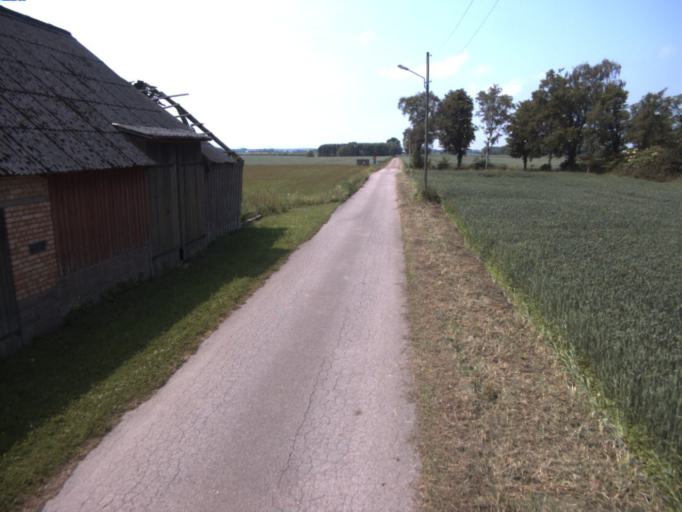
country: SE
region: Skane
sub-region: Angelholms Kommun
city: Strovelstorp
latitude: 56.1434
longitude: 12.7695
